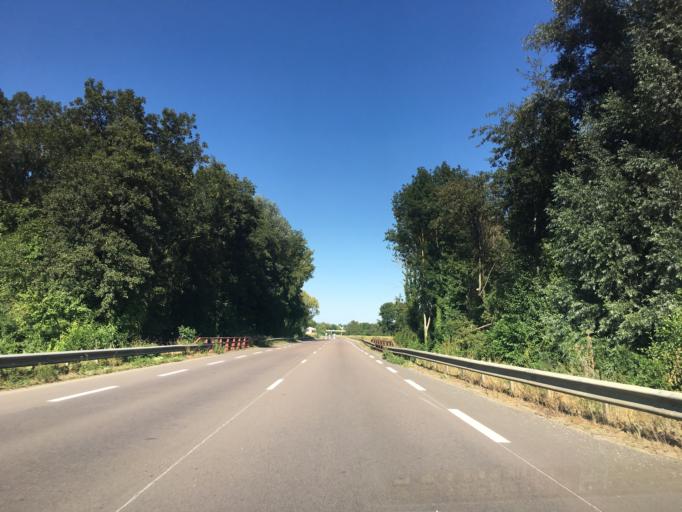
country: FR
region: Bourgogne
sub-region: Departement de l'Yonne
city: Maillot
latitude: 48.1805
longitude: 3.3011
